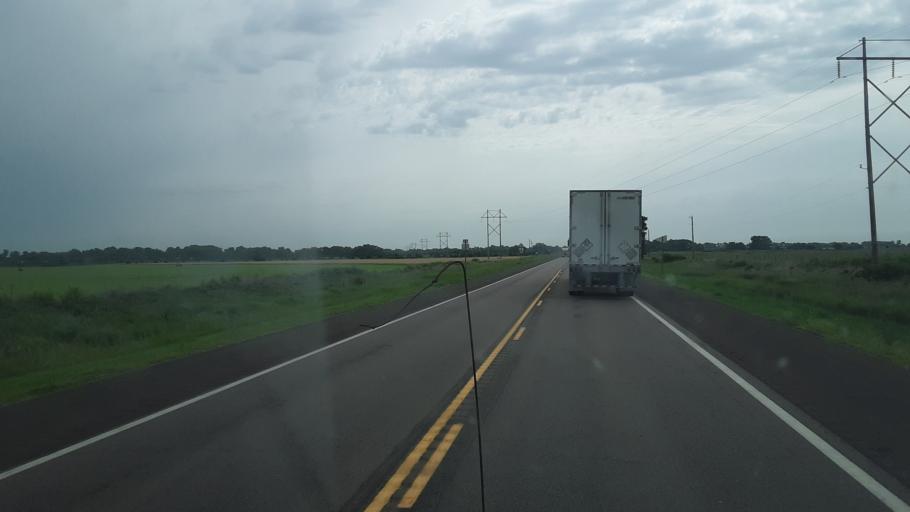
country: US
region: Kansas
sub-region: Stafford County
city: Saint John
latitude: 37.9558
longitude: -98.7423
